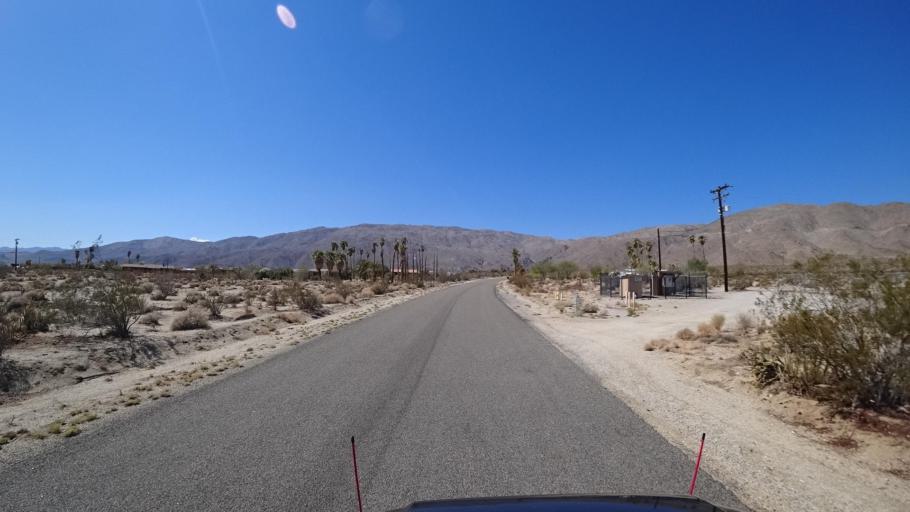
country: US
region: California
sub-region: San Diego County
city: Borrego Springs
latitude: 33.2316
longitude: -116.3882
